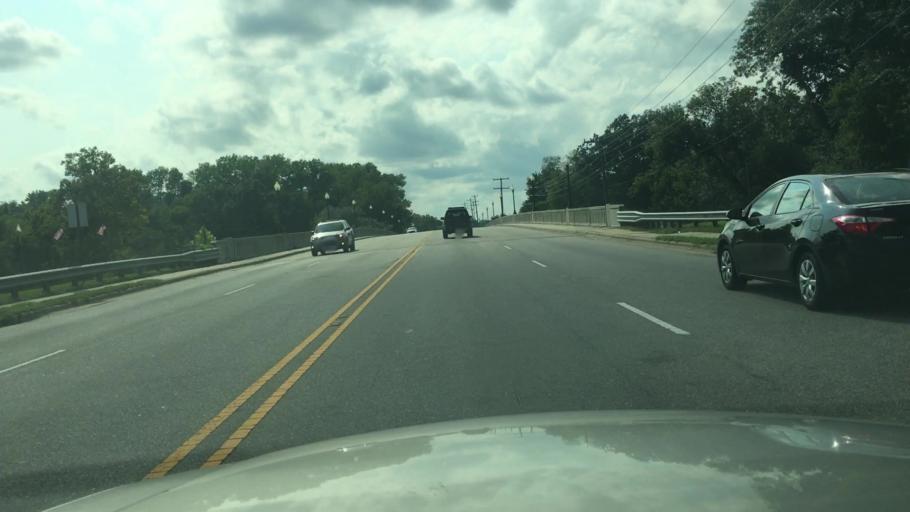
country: US
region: North Carolina
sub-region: Cumberland County
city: Fayetteville
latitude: 35.0470
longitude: -78.8567
